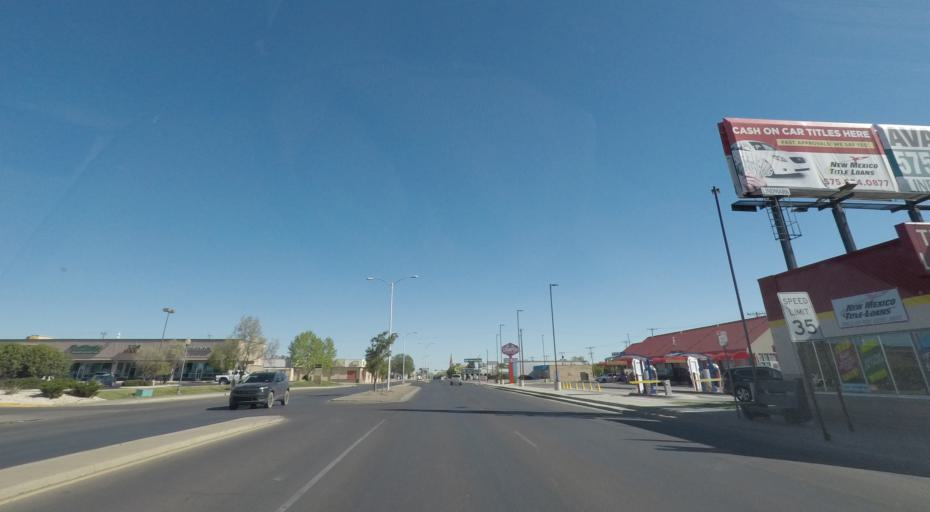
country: US
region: New Mexico
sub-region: Chaves County
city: Roswell
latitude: 33.3806
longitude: -104.5227
